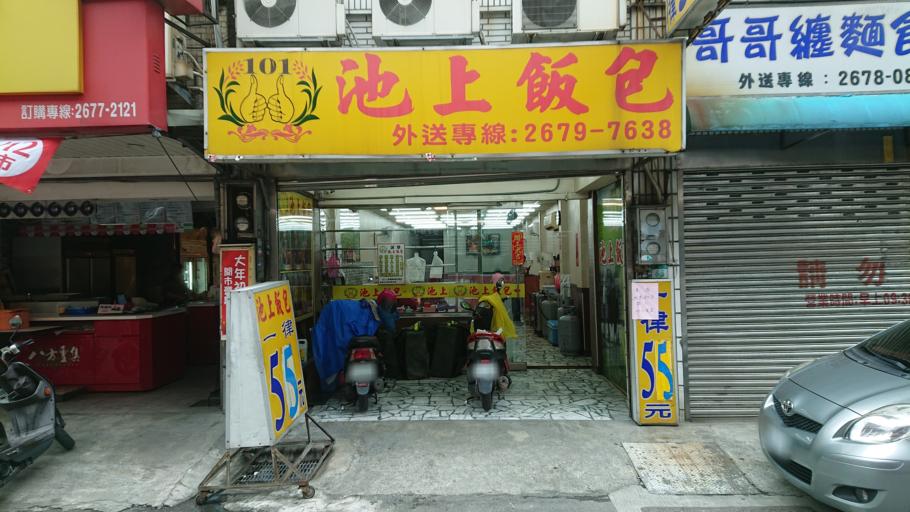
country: TW
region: Taiwan
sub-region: Taoyuan
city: Taoyuan
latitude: 24.9553
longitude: 121.3499
